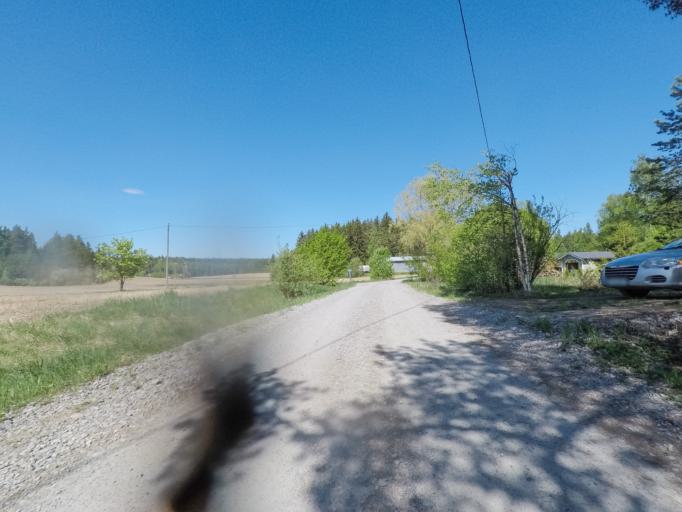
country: FI
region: Pirkanmaa
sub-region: Etelae-Pirkanmaa
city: Kylmaekoski
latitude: 61.1607
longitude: 23.7093
